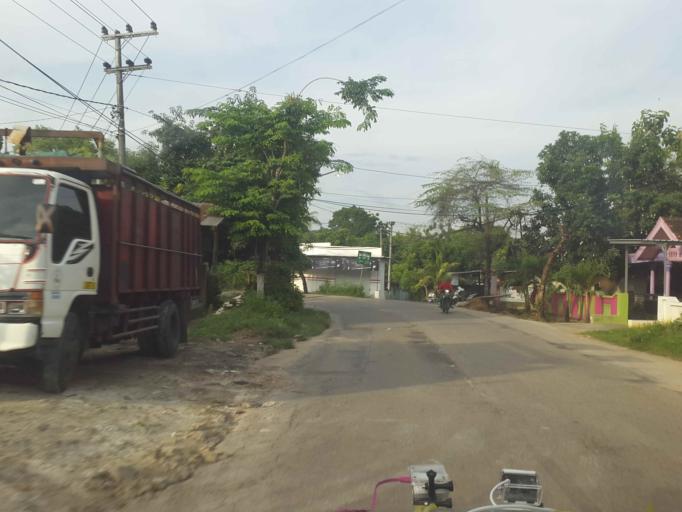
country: ID
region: East Java
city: Senmasen
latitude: -6.9963
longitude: 113.8669
